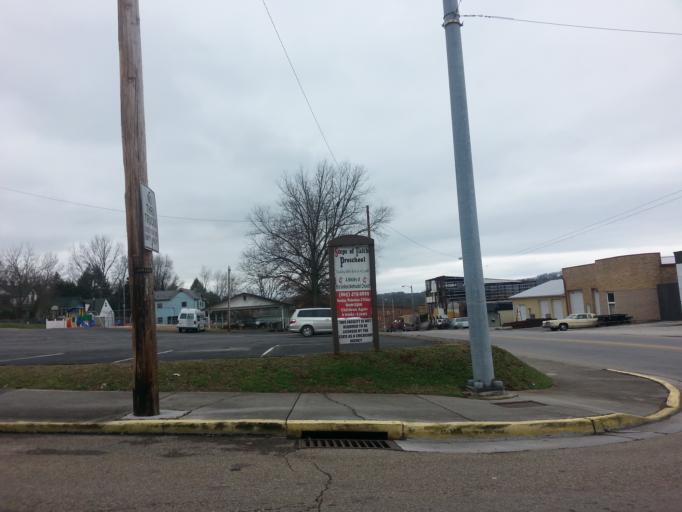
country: US
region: Tennessee
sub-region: Jefferson County
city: Jefferson City
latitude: 36.1259
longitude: -83.4900
